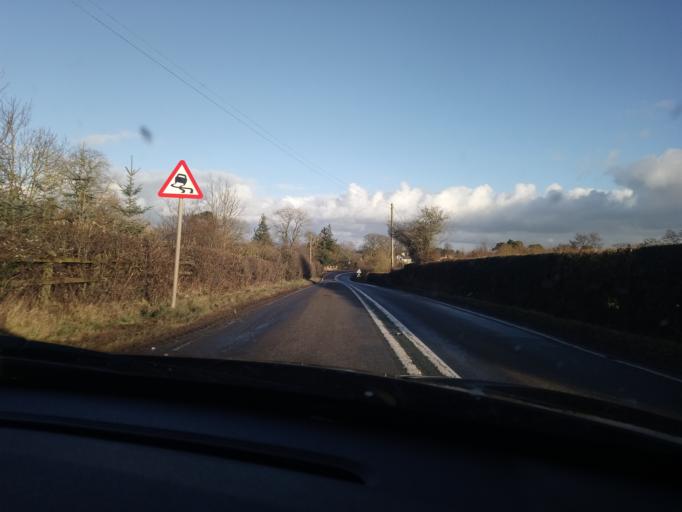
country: GB
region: Wales
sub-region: Wrexham
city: Overton
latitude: 52.9275
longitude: -2.9555
